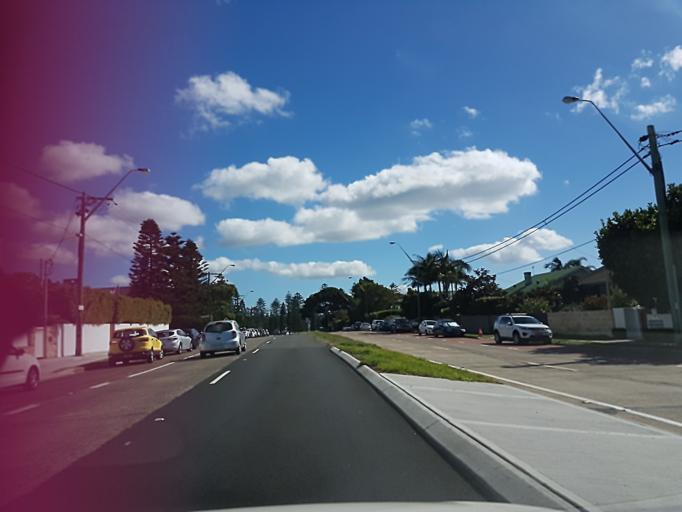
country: AU
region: New South Wales
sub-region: Warringah
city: Dee Why
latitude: -33.7365
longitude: 151.3024
